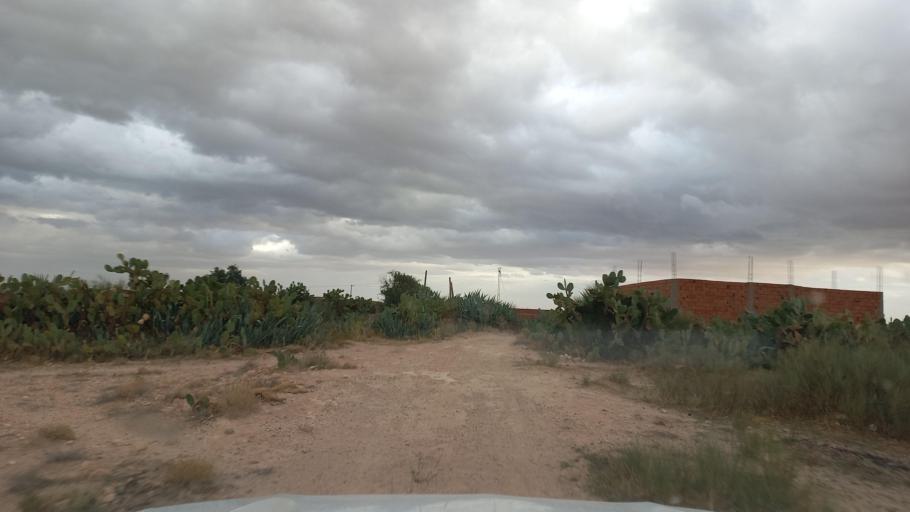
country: TN
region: Al Qasrayn
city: Kasserine
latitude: 35.2743
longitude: 8.9368
